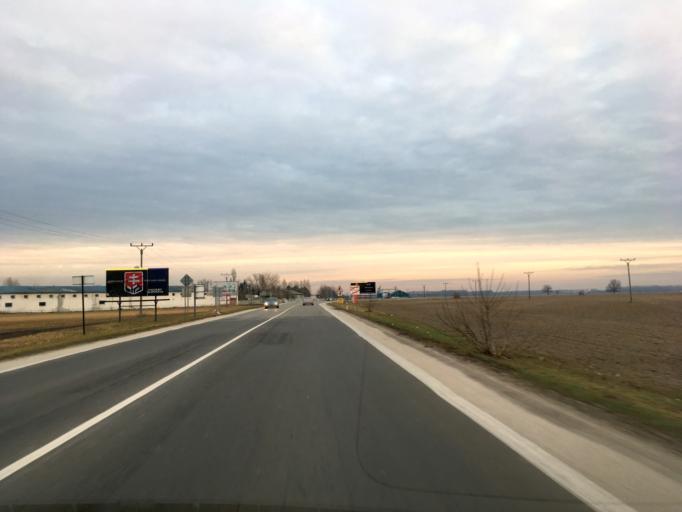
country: SK
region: Trnavsky
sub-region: Okres Dunajska Streda
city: Velky Meder
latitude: 47.9356
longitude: 17.7208
